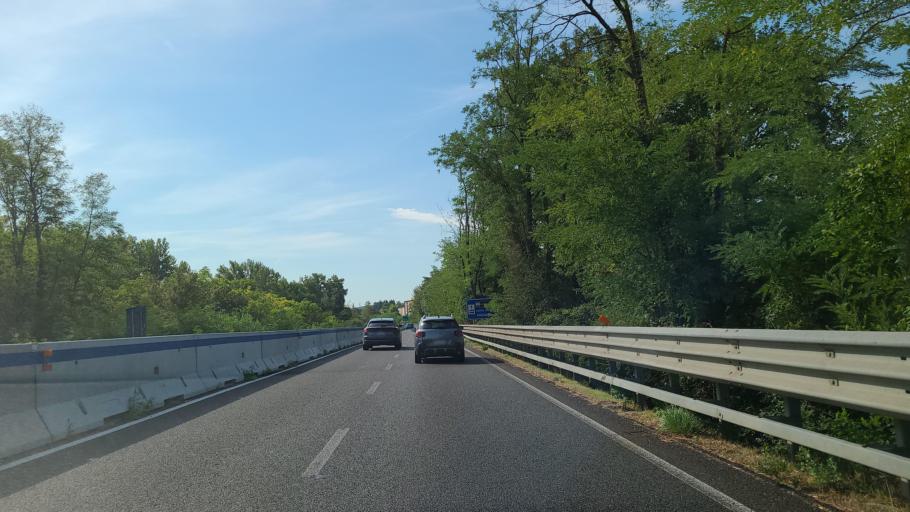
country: IT
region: Tuscany
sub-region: Province of Florence
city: Sambuca
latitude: 43.6010
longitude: 11.1929
